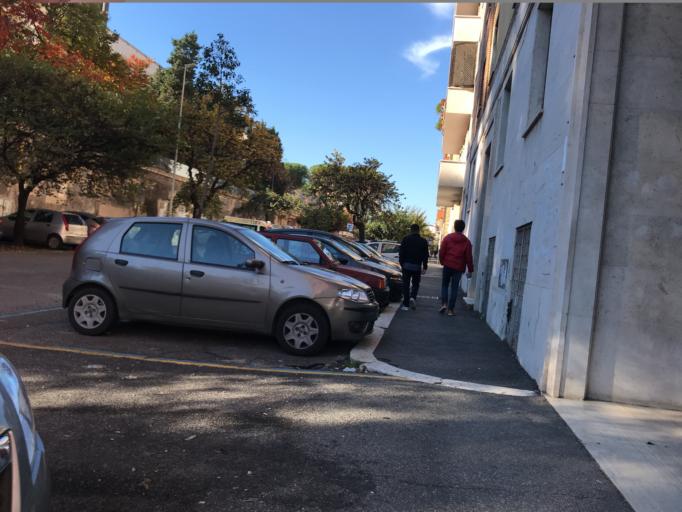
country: IT
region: Latium
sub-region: Citta metropolitana di Roma Capitale
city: Rome
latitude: 41.9073
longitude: 12.5157
